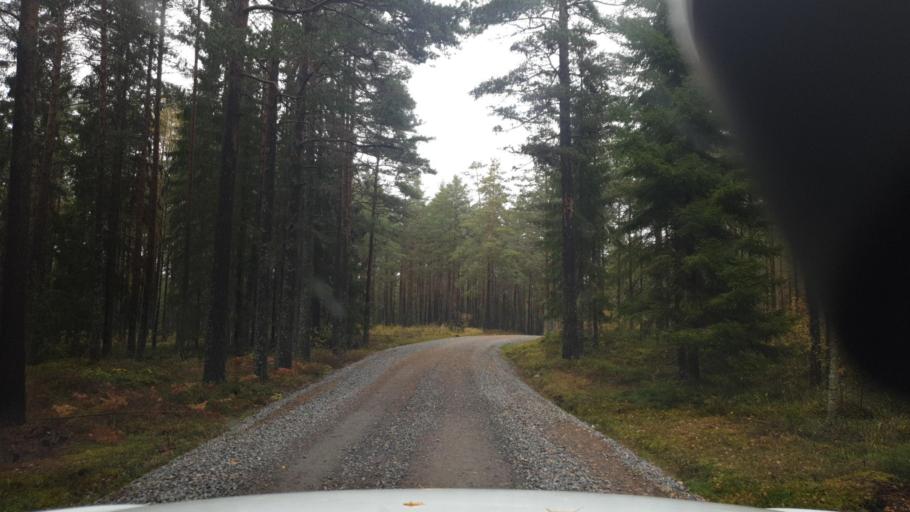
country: SE
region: Vaermland
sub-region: Karlstads Kommun
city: Edsvalla
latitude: 59.4567
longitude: 13.0978
